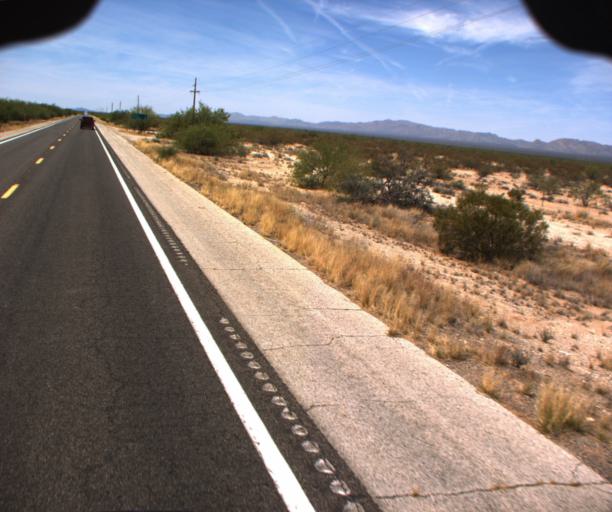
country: US
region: Arizona
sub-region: La Paz County
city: Salome
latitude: 33.8912
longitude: -113.3326
